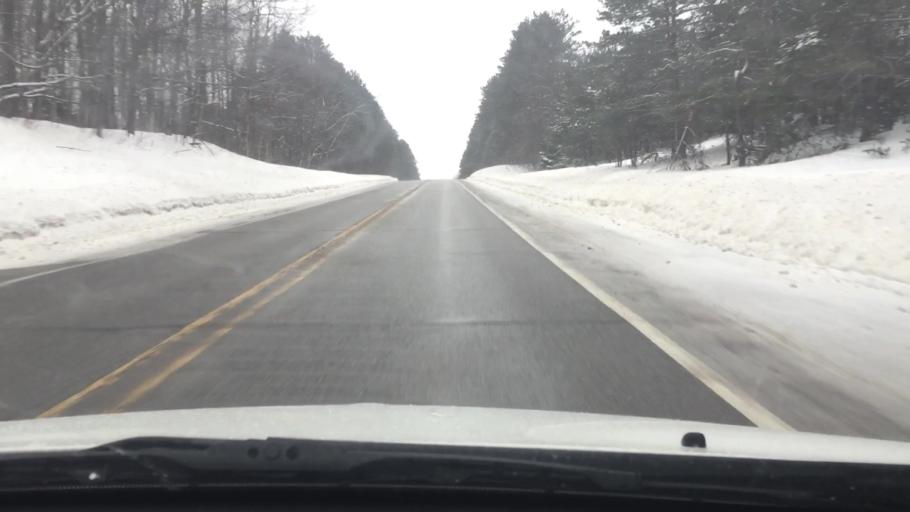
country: US
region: Michigan
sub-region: Otsego County
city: Gaylord
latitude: 45.0617
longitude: -84.8050
